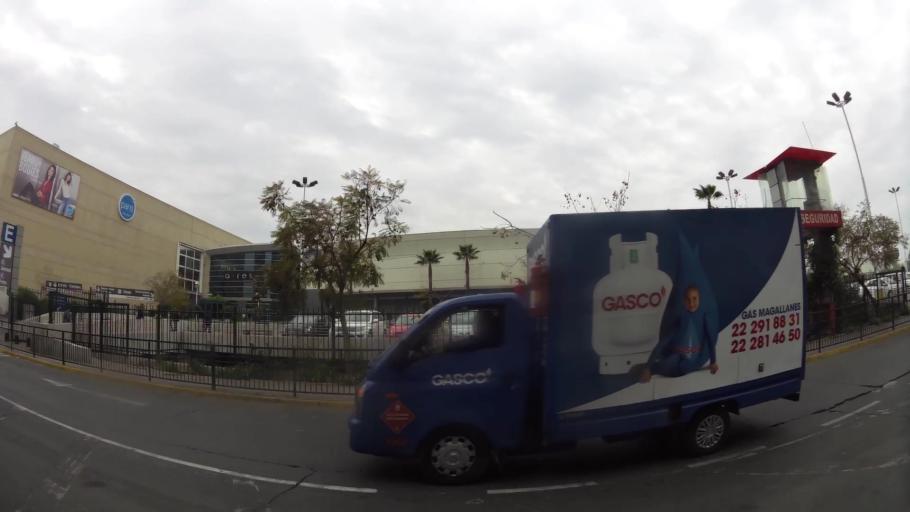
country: CL
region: Santiago Metropolitan
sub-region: Provincia de Santiago
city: Villa Presidente Frei, Nunoa, Santiago, Chile
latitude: -33.5167
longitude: -70.5998
